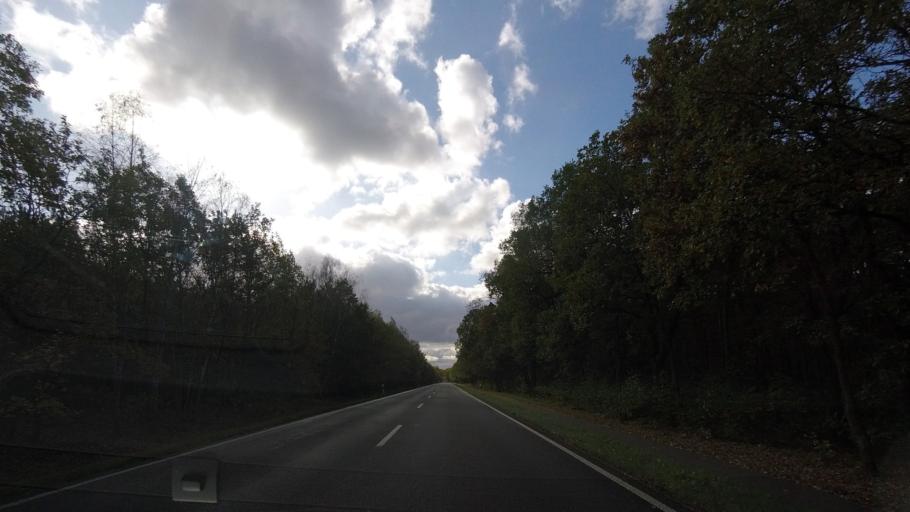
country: DE
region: Brandenburg
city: Treuenbrietzen
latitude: 52.1142
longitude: 12.8901
